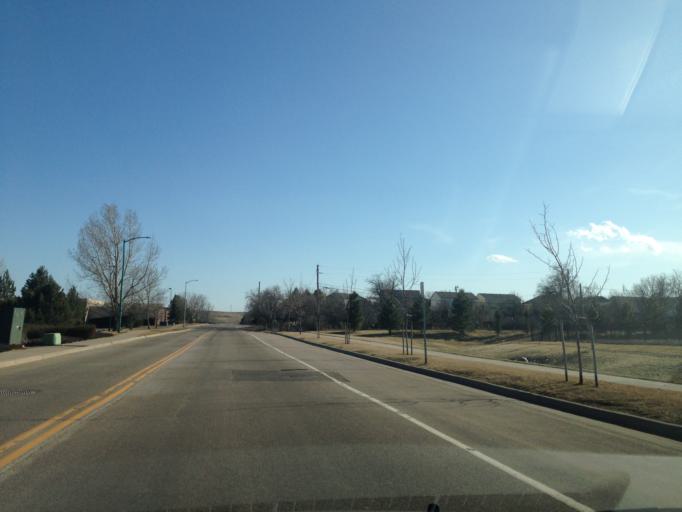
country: US
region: Colorado
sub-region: Boulder County
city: Superior
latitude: 39.9591
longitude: -105.1753
